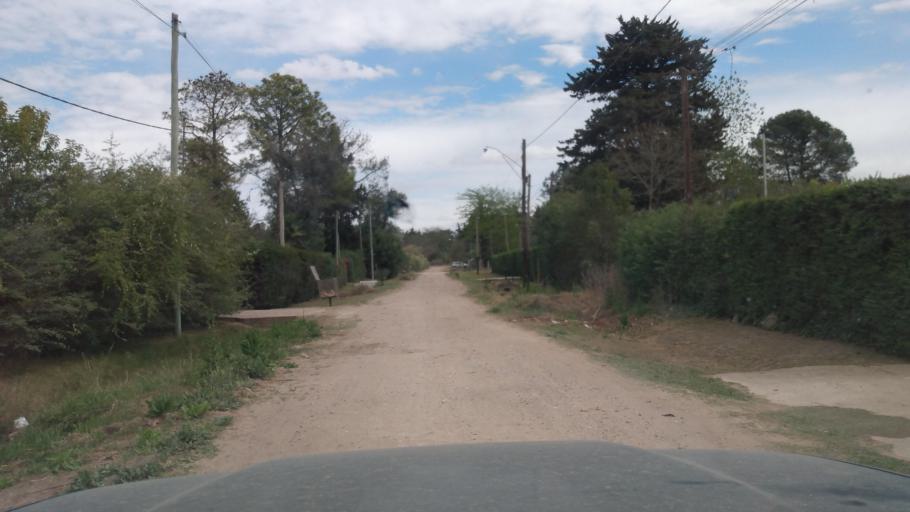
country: AR
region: Buenos Aires
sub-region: Partido de Lujan
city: Lujan
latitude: -34.5904
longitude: -59.1318
